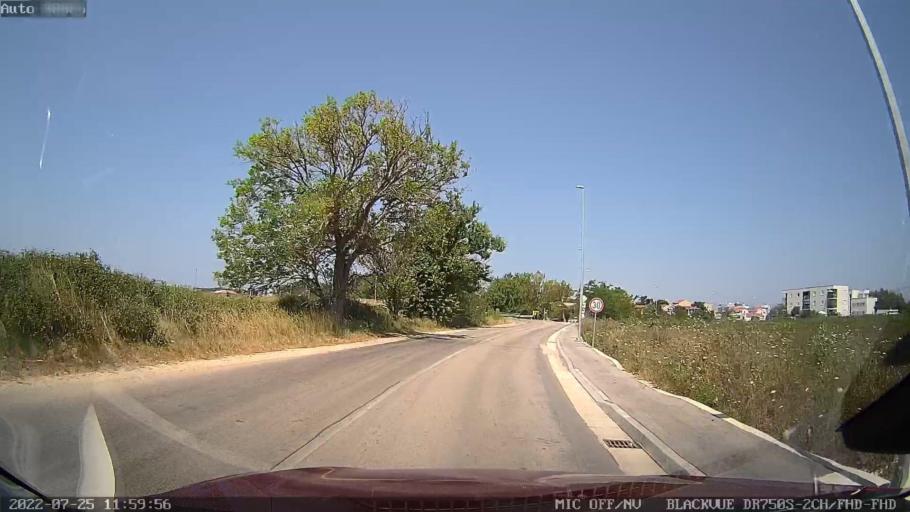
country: HR
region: Zadarska
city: Nin
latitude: 44.2427
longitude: 15.1969
